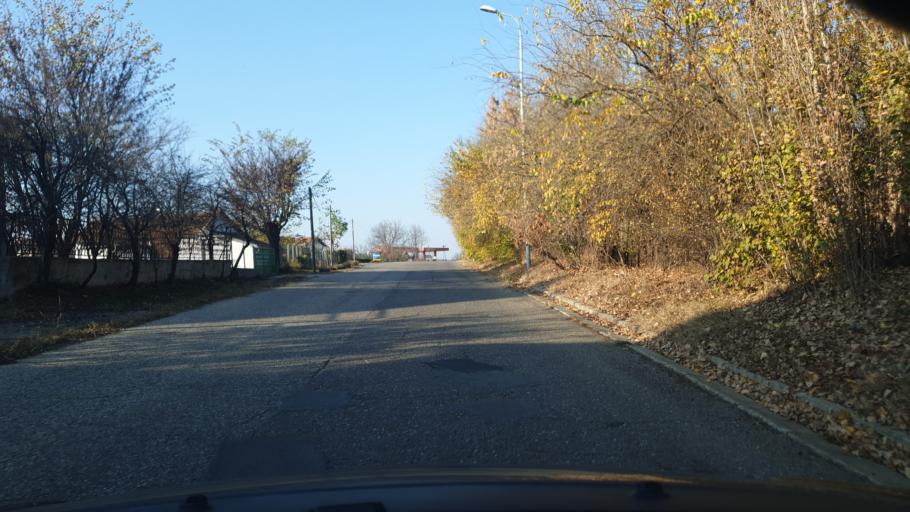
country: RS
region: Central Serbia
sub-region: Borski Okrug
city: Negotin
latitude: 44.2388
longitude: 22.5177
